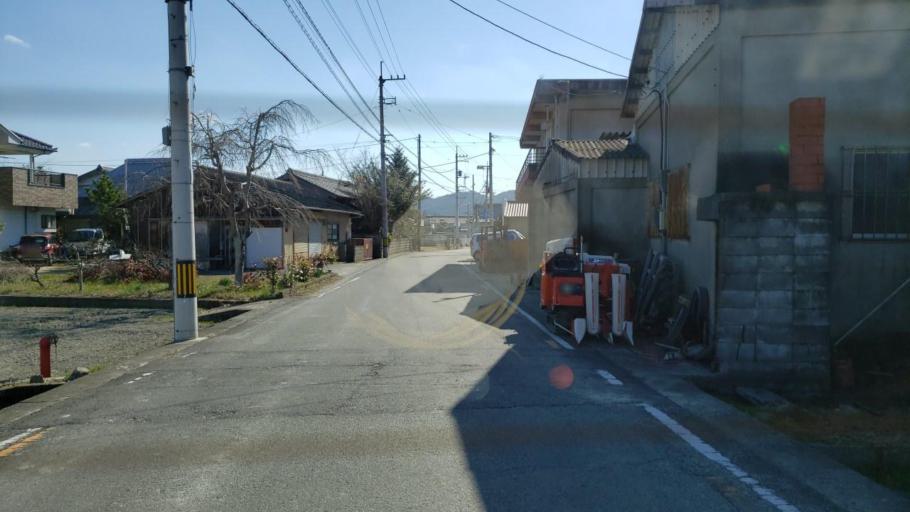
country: JP
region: Tokushima
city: Ishii
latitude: 34.0761
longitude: 134.4291
